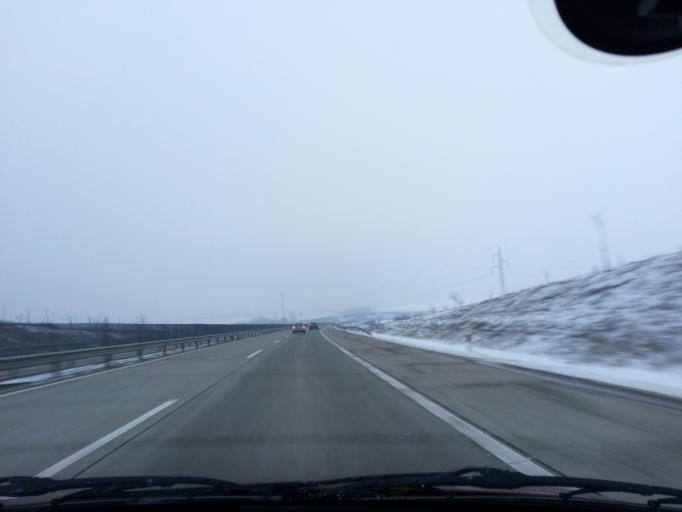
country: HU
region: Pest
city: Kerepes
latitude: 47.5478
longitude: 19.3134
